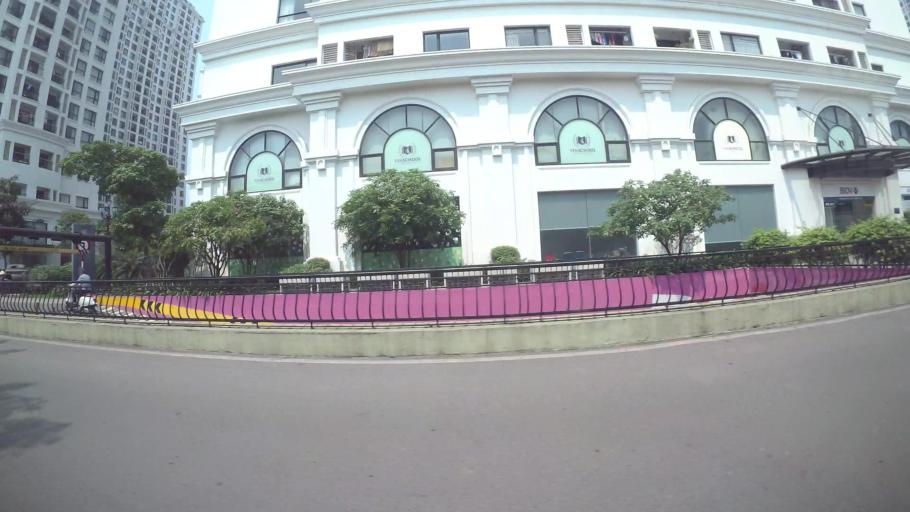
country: VN
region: Ha Noi
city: Thanh Xuan
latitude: 21.0024
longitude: 105.8138
